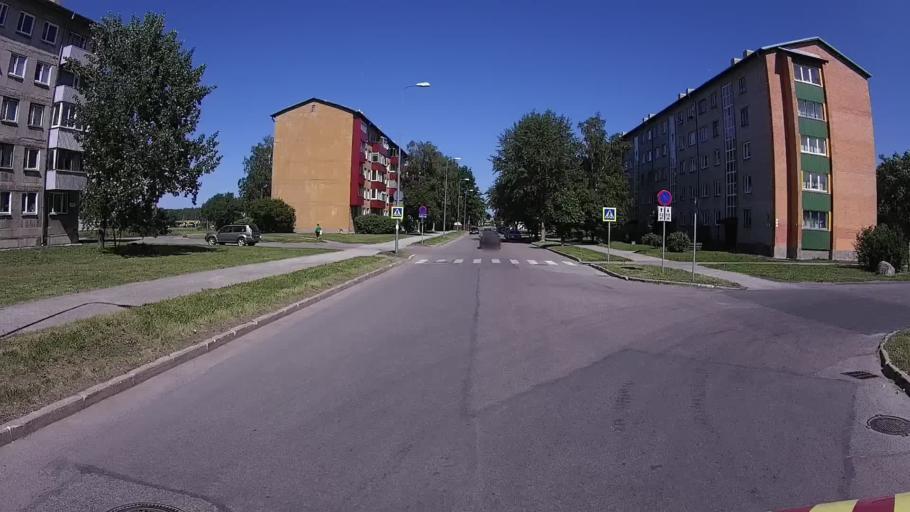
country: EE
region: Ida-Virumaa
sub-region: Kohtla-Jaerve linn
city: Kohtla-Jarve
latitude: 59.4076
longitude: 27.2896
